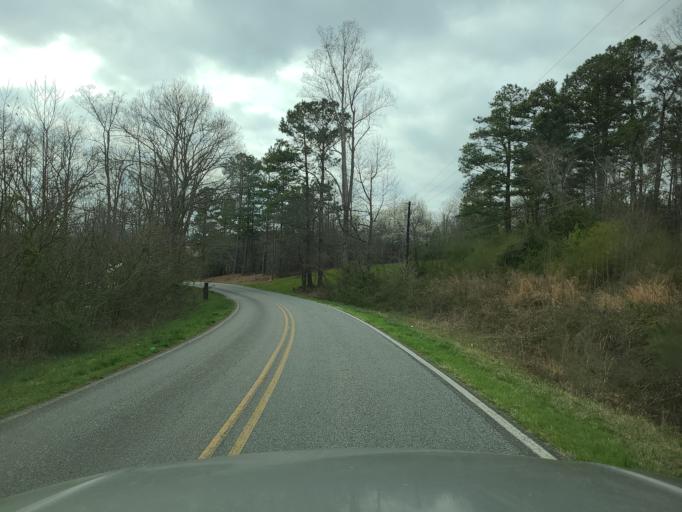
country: US
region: North Carolina
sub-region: Cleveland County
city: Boiling Springs
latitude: 35.2572
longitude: -81.6901
